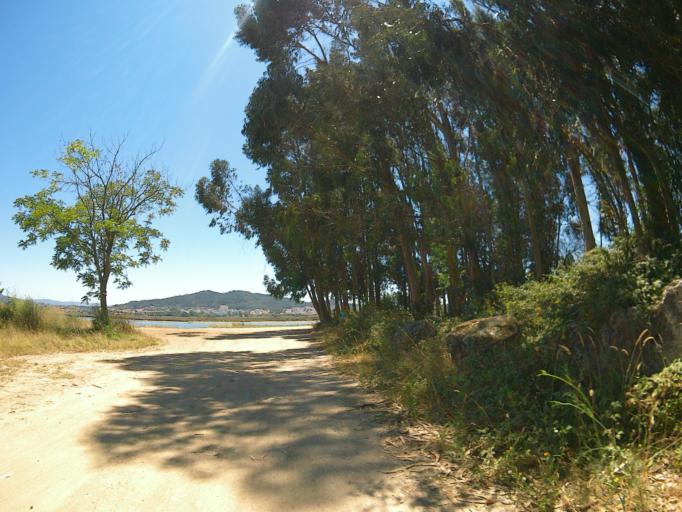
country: PT
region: Viana do Castelo
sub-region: Viana do Castelo
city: Meadela
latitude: 41.6985
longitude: -8.8045
